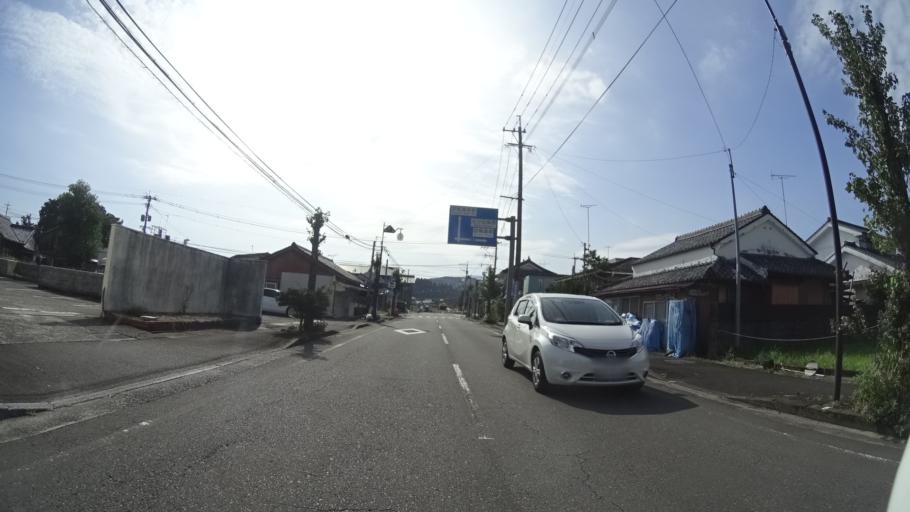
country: JP
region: Kagoshima
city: Okuchi-shinohara
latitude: 32.0463
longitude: 130.7660
